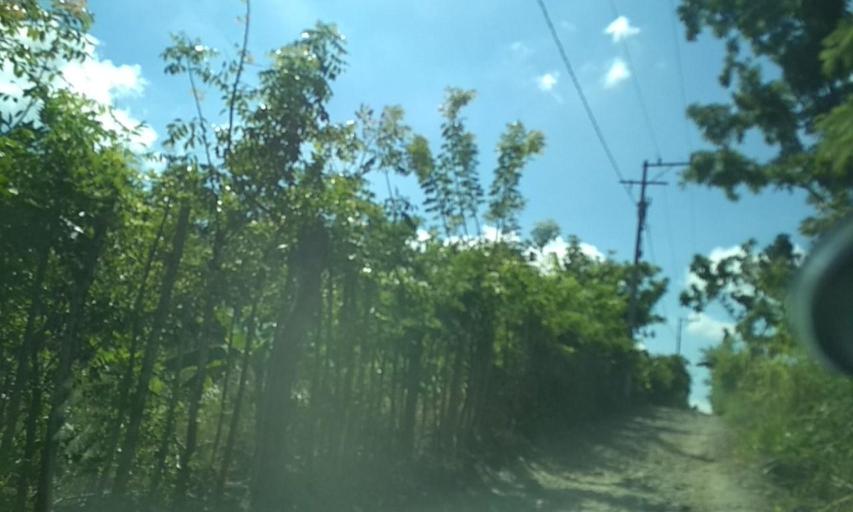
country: MX
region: Veracruz
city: Cazones de Herrera
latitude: 20.6232
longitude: -97.3266
